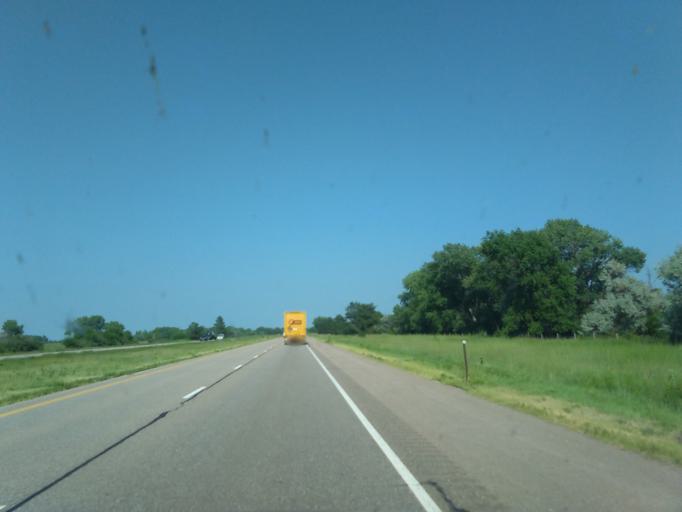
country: US
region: Nebraska
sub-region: Buffalo County
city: Gibbon
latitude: 40.7178
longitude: -98.7835
